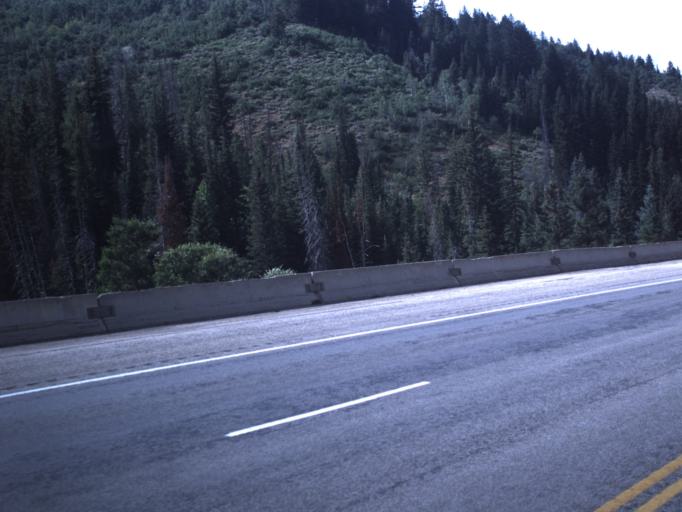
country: US
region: Utah
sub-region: Wasatch County
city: Heber
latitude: 40.3250
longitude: -111.2619
